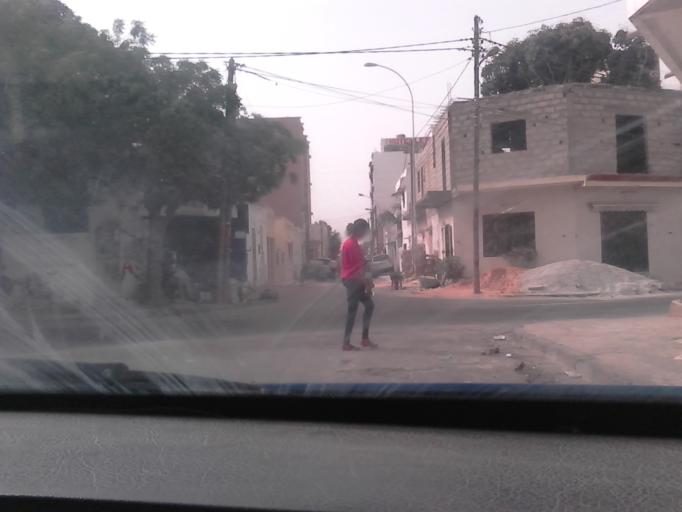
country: SN
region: Dakar
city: Dakar
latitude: 14.7008
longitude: -17.4529
